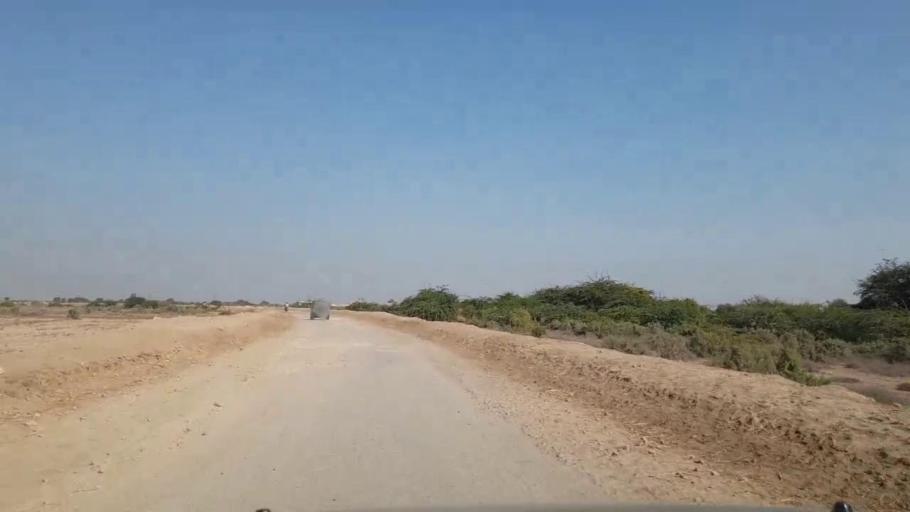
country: PK
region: Sindh
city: Digri
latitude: 24.9598
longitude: 69.1128
